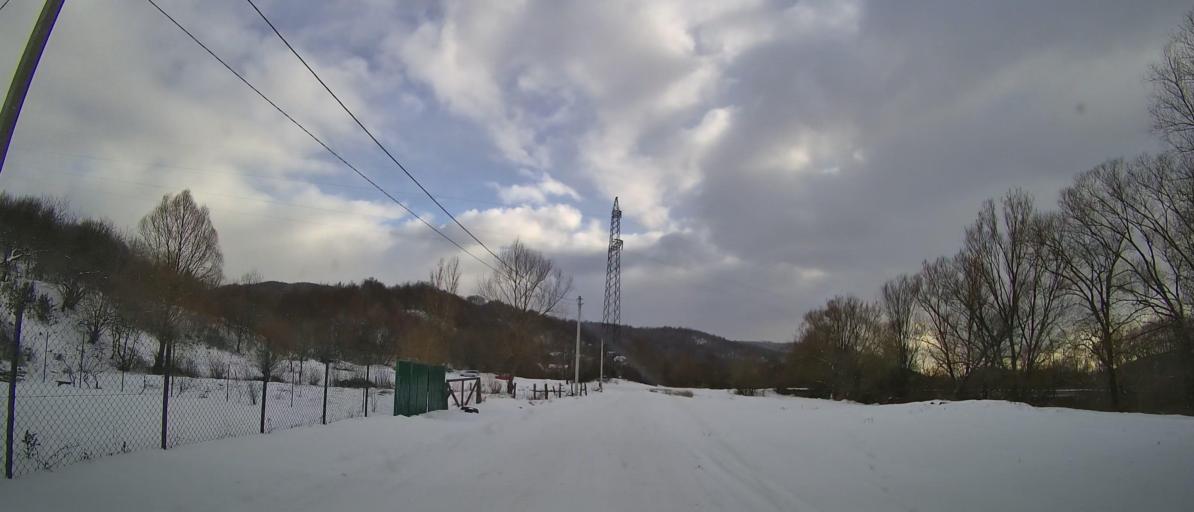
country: UA
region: Zakarpattia
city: Velykyi Bereznyi
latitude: 48.9088
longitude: 22.4676
